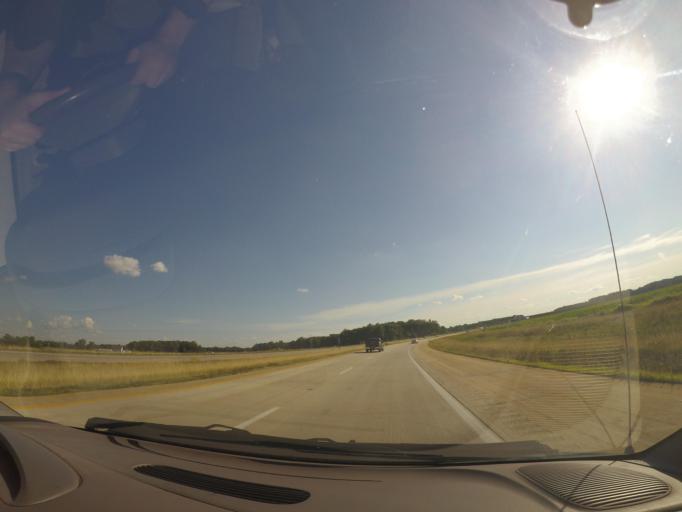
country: US
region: Ohio
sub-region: Lucas County
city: Whitehouse
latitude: 41.4421
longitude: -83.8459
